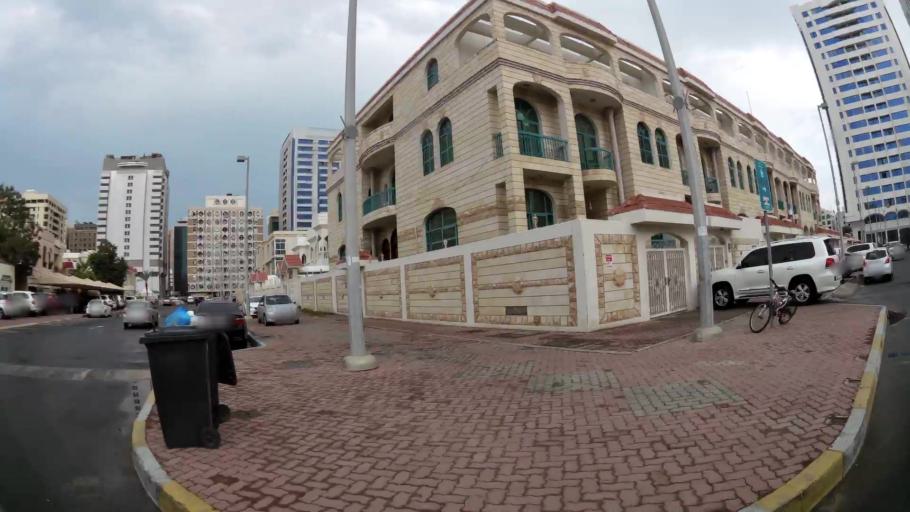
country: AE
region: Abu Dhabi
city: Abu Dhabi
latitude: 24.4878
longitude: 54.3698
